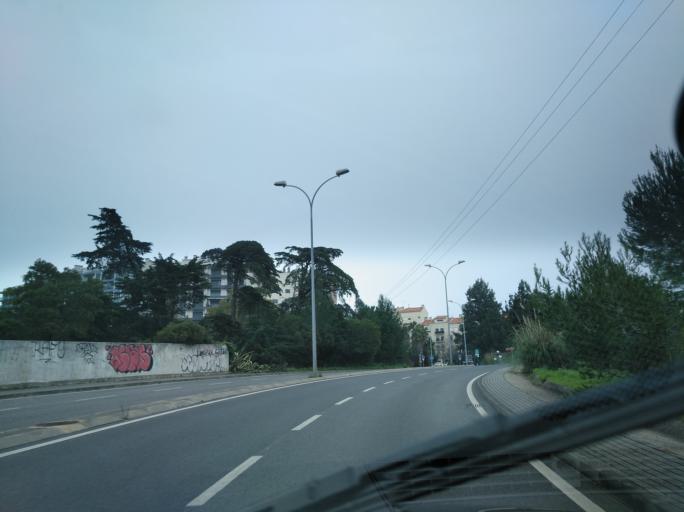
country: PT
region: Lisbon
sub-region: Odivelas
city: Odivelas
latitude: 38.7858
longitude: -9.1949
